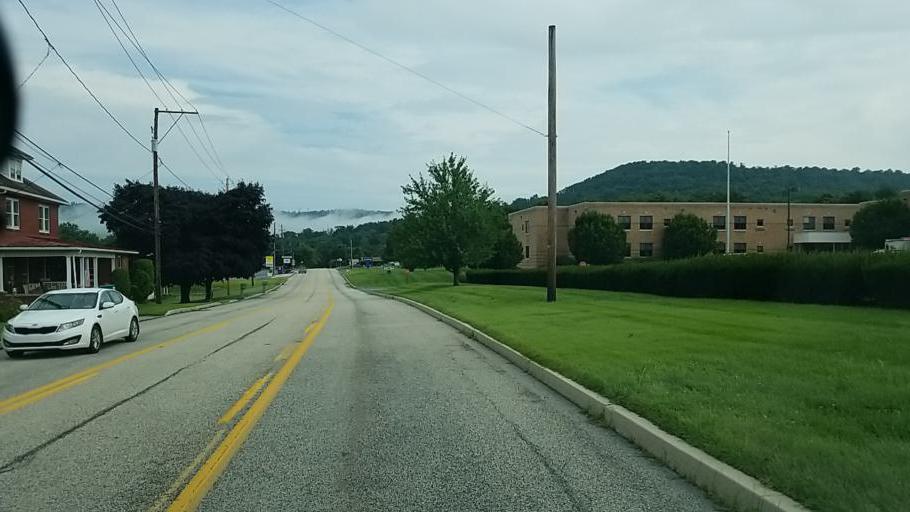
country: US
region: Pennsylvania
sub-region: Perry County
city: Marysville
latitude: 40.3788
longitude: -76.9325
